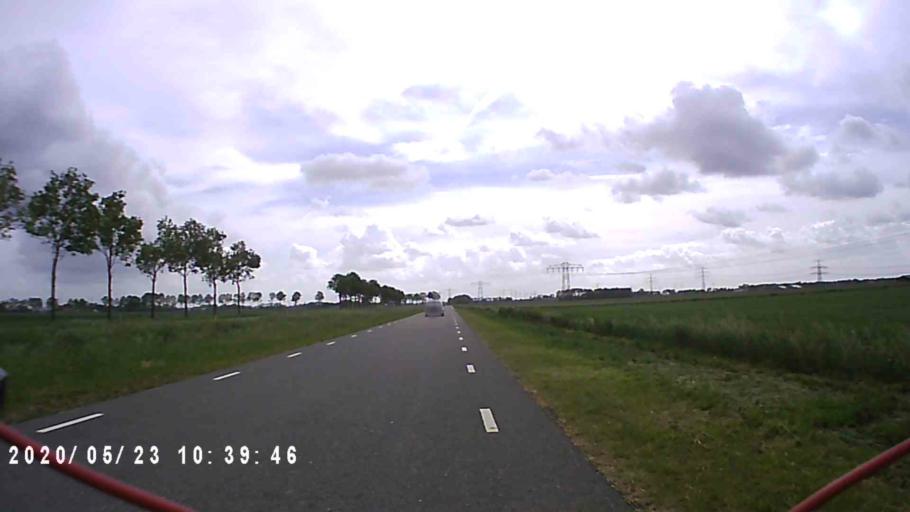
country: NL
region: Groningen
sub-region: Gemeente Appingedam
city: Appingedam
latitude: 53.3028
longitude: 6.8871
